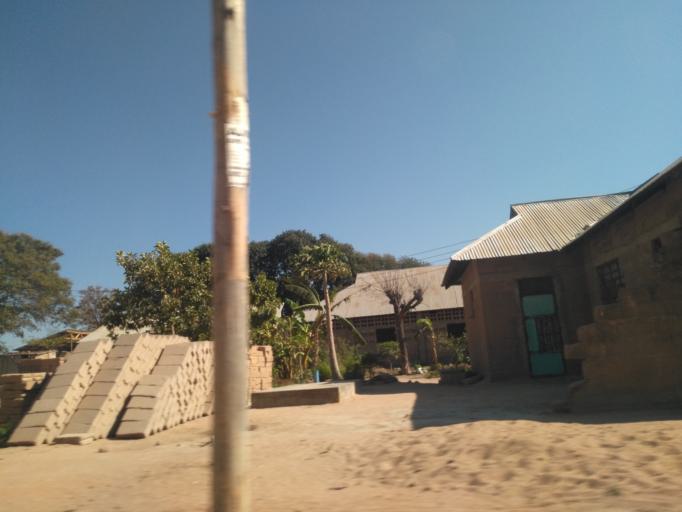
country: TZ
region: Dodoma
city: Dodoma
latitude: -6.1394
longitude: 35.7460
